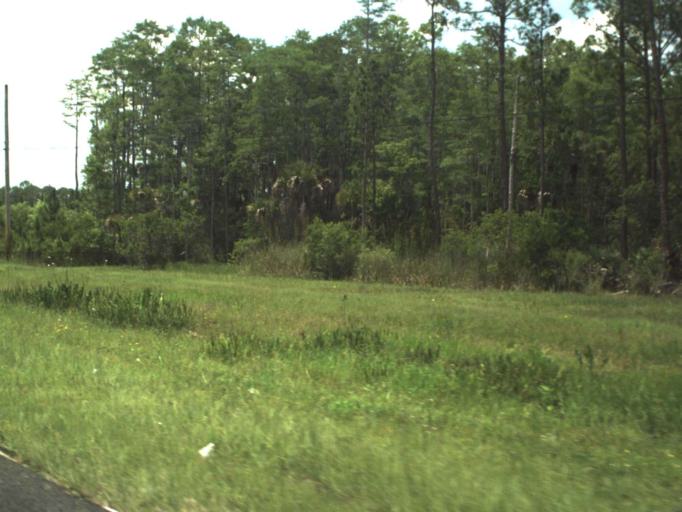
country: US
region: Florida
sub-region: Volusia County
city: Glencoe
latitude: 29.0124
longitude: -81.0105
